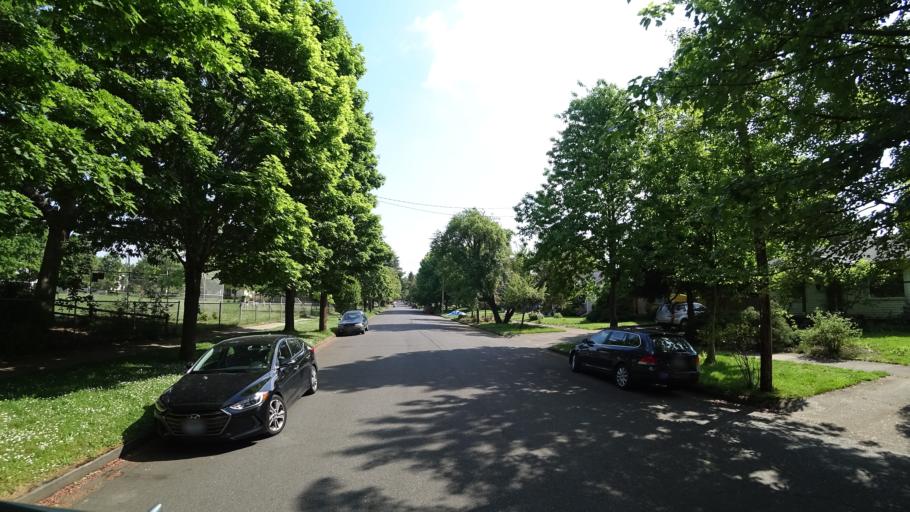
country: US
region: Oregon
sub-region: Multnomah County
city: Portland
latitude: 45.5517
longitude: -122.6483
